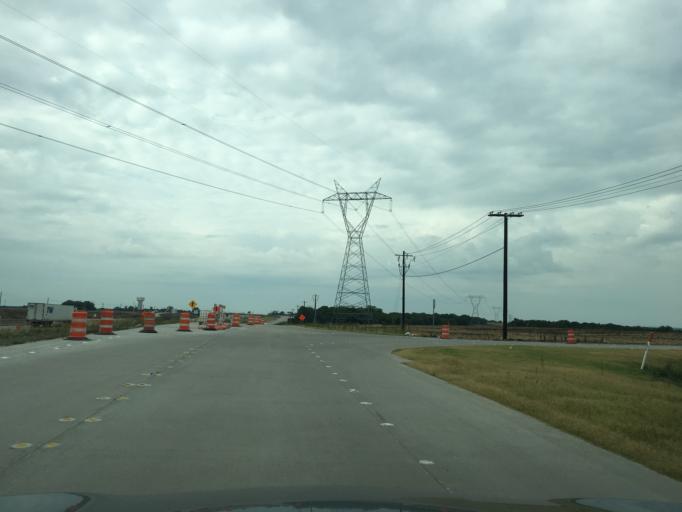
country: US
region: Texas
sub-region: Collin County
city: Anna
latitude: 33.3706
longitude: -96.5825
